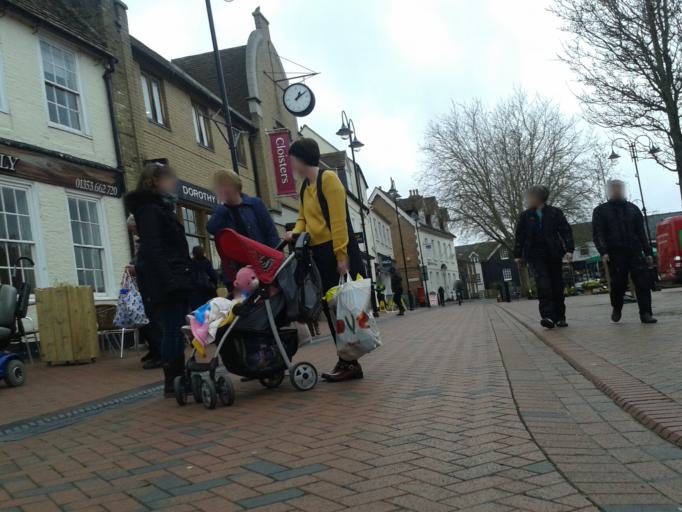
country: GB
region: England
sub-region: Cambridgeshire
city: Ely
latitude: 52.3994
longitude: 0.2662
